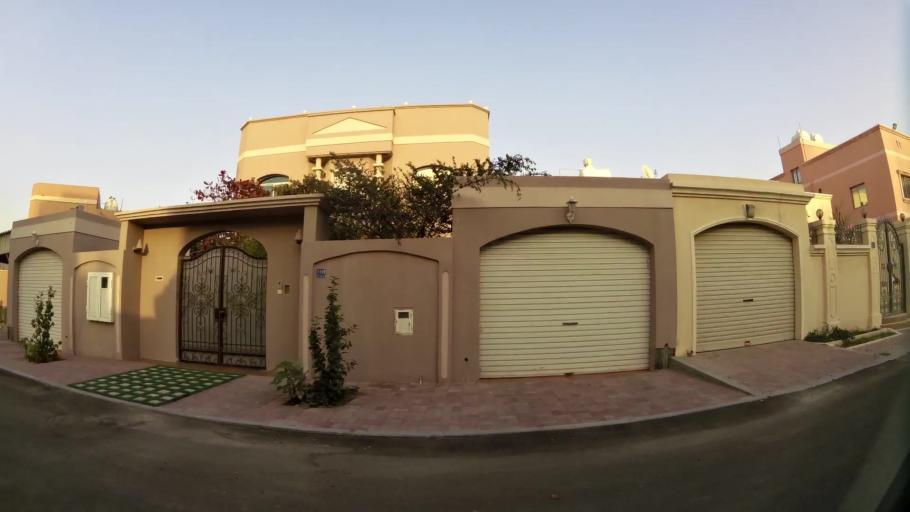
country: BH
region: Northern
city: Madinat `Isa
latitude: 26.1883
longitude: 50.4770
